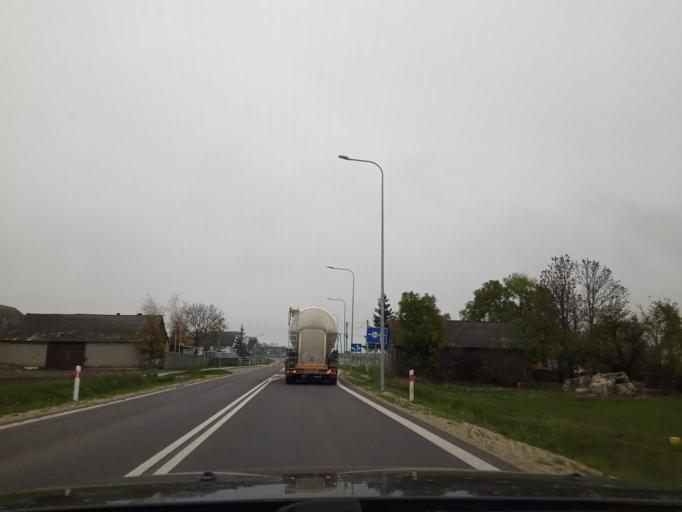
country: PL
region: Swietokrzyskie
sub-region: Powiat jedrzejowski
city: Jedrzejow
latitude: 50.5895
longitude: 20.3214
